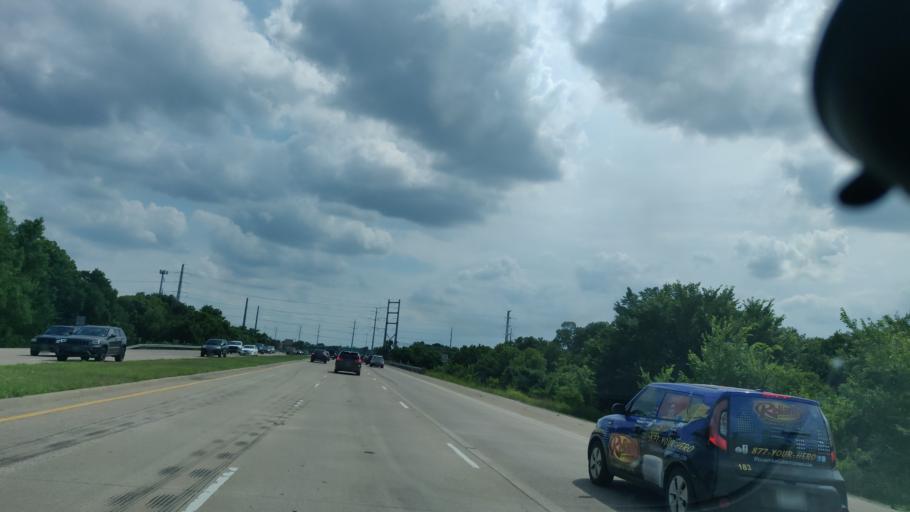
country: US
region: Texas
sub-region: Dallas County
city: Sachse
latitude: 32.9618
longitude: -96.6133
